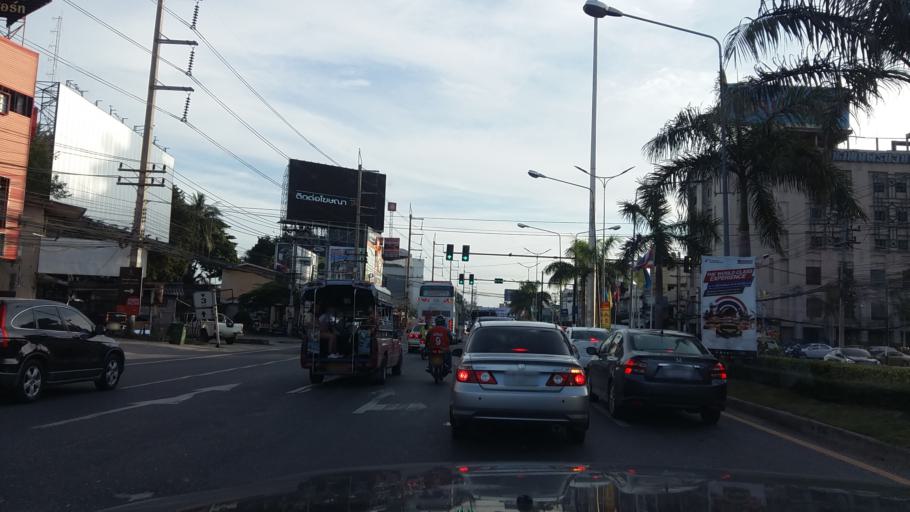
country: TH
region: Chon Buri
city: Chon Buri
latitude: 13.2870
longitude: 100.9395
